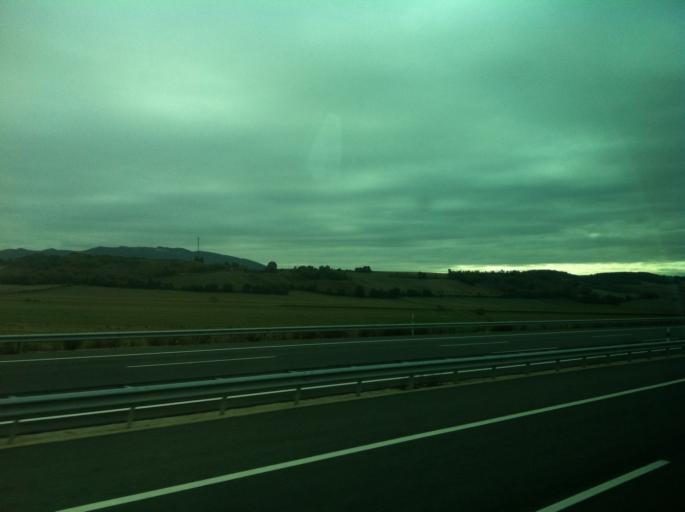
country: ES
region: Basque Country
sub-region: Provincia de Alava
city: Arminon
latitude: 42.7119
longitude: -2.8687
